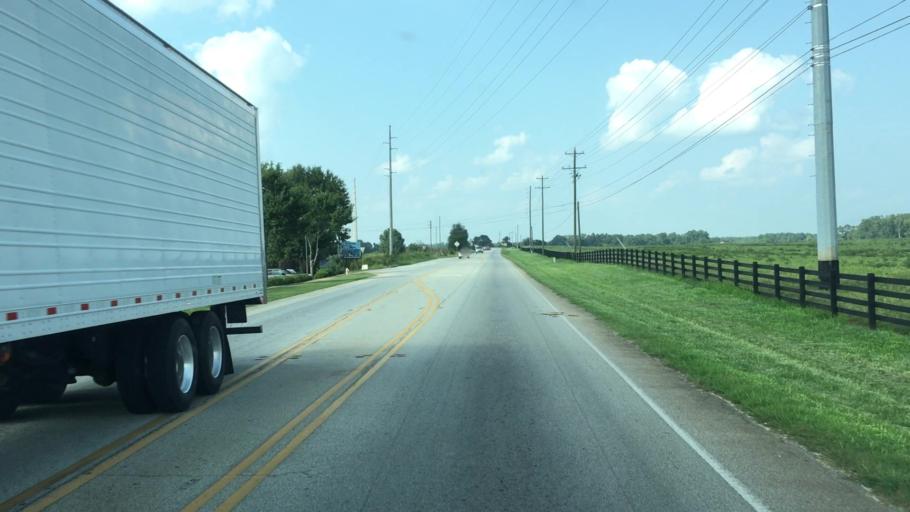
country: US
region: Georgia
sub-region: Walton County
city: Social Circle
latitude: 33.5531
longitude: -83.7386
